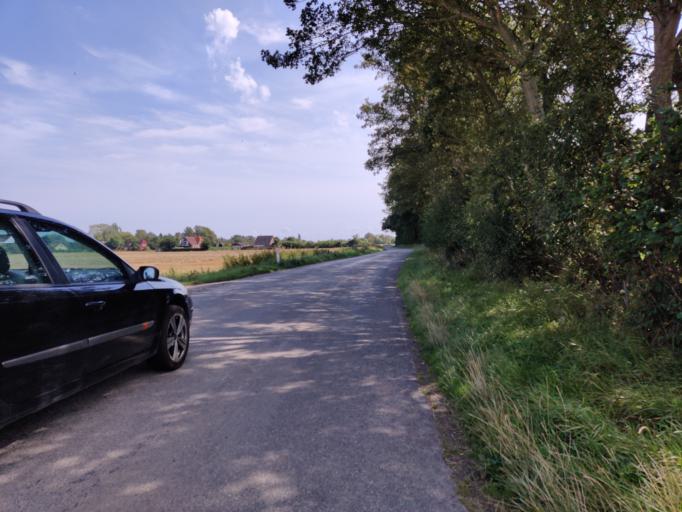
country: DK
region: Zealand
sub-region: Guldborgsund Kommune
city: Nykobing Falster
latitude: 54.6460
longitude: 11.8916
